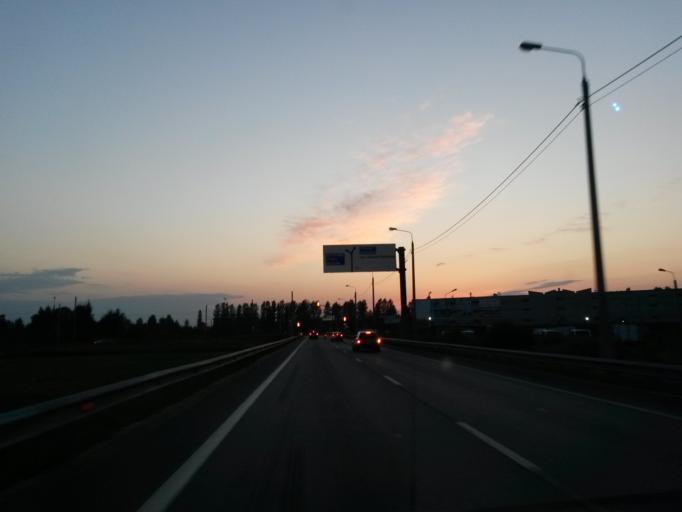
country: RU
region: Jaroslavl
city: Yaroslavl
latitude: 57.6711
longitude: 39.7770
